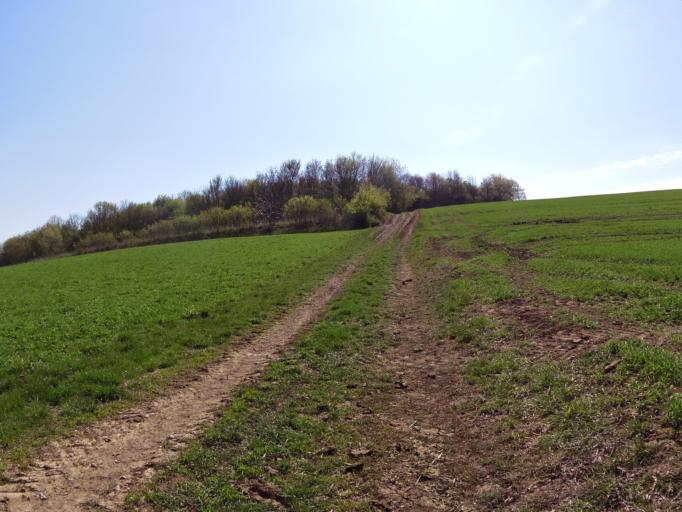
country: DE
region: Bavaria
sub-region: Regierungsbezirk Unterfranken
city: Biebelried
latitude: 49.7864
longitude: 10.0679
